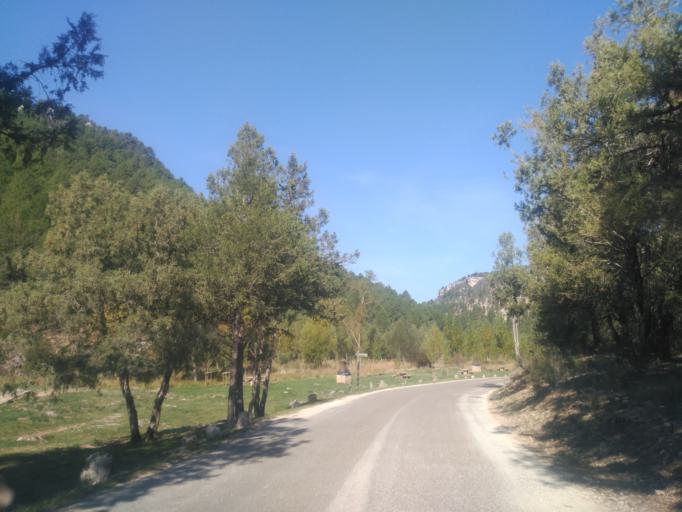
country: ES
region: Castille and Leon
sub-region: Provincia de Soria
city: Ucero
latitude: 41.7342
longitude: -3.0481
